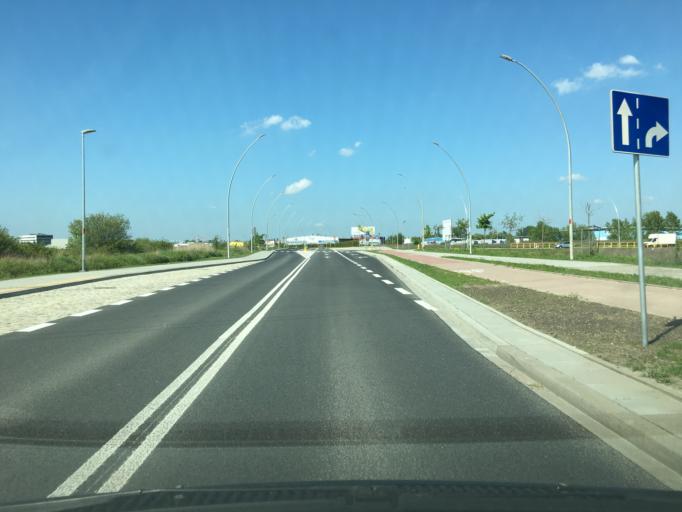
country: PL
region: Lower Silesian Voivodeship
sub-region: Powiat wroclawski
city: Bielany Wroclawskie
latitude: 51.0643
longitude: 16.9574
